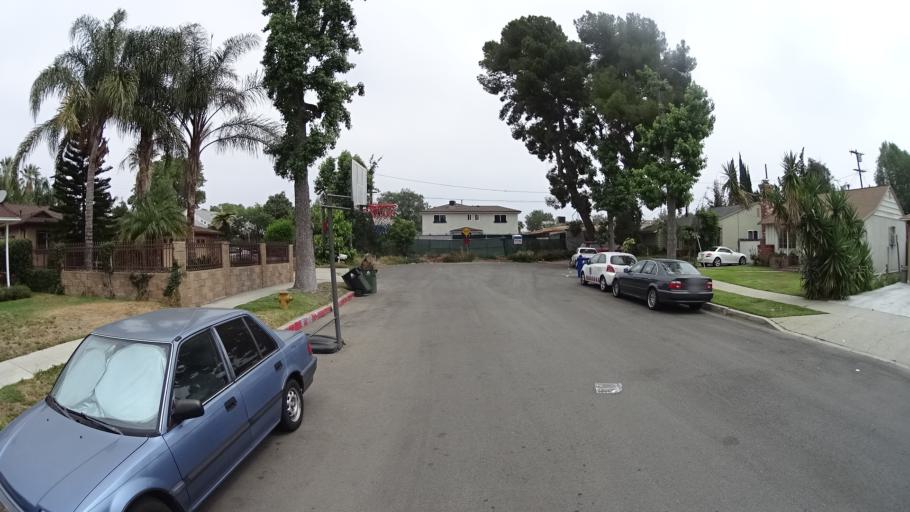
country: US
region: California
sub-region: Los Angeles County
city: North Hollywood
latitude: 34.1913
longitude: -118.4065
